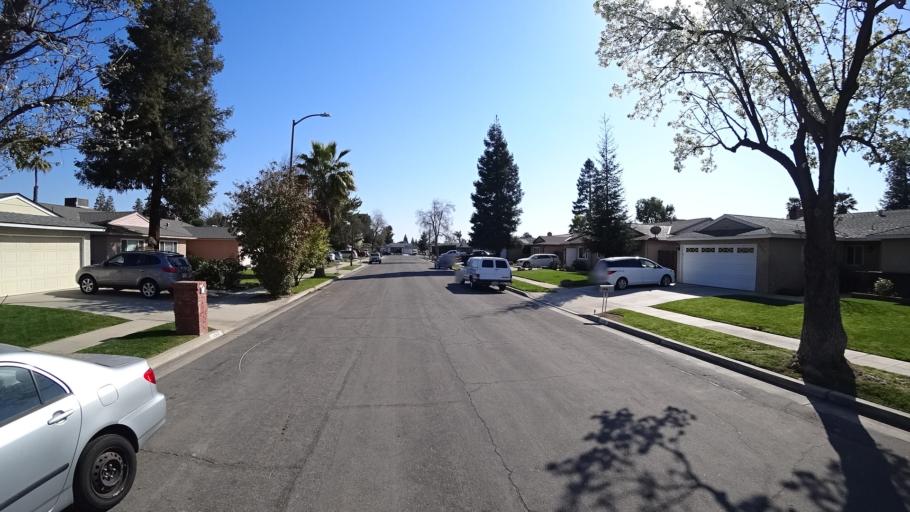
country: US
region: California
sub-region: Fresno County
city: Fresno
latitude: 36.8426
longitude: -119.8194
